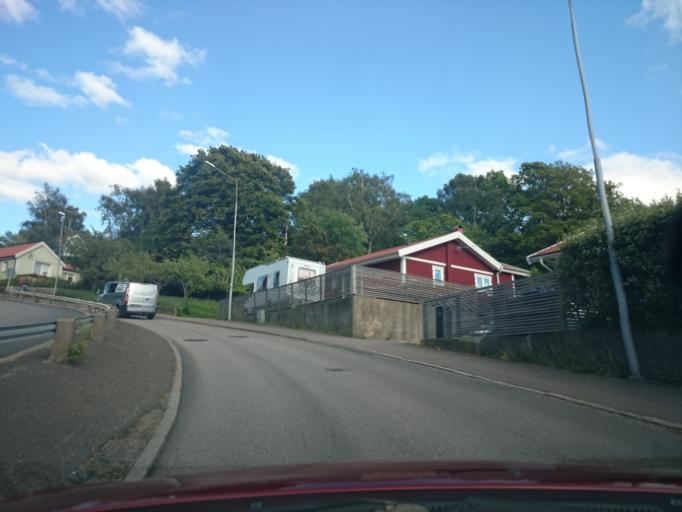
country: SE
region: Vaestra Goetaland
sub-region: Molndal
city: Moelndal
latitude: 57.6638
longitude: 12.0282
